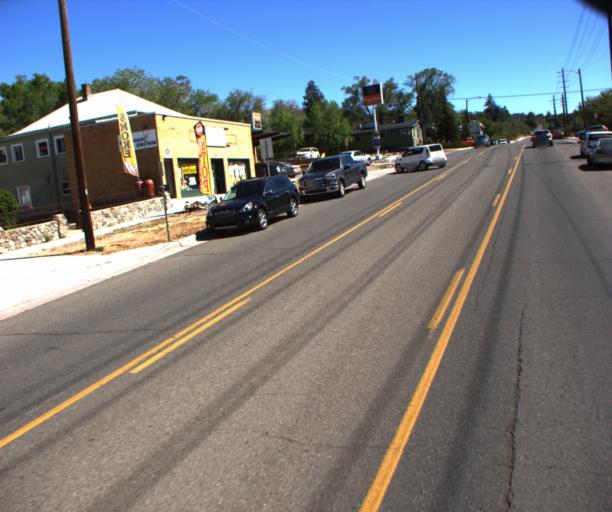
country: US
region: Arizona
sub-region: Yavapai County
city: Prescott
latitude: 34.5350
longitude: -112.4703
